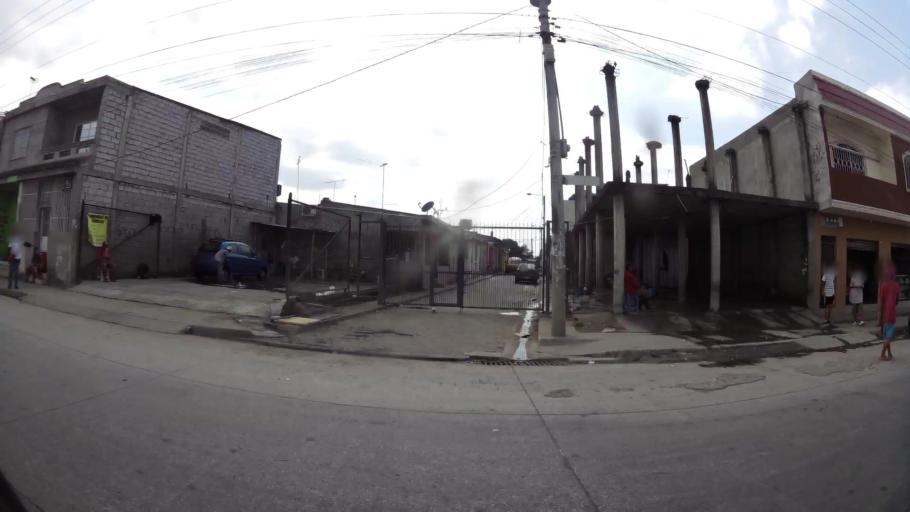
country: EC
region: Guayas
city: Eloy Alfaro
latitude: -2.0871
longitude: -79.9246
